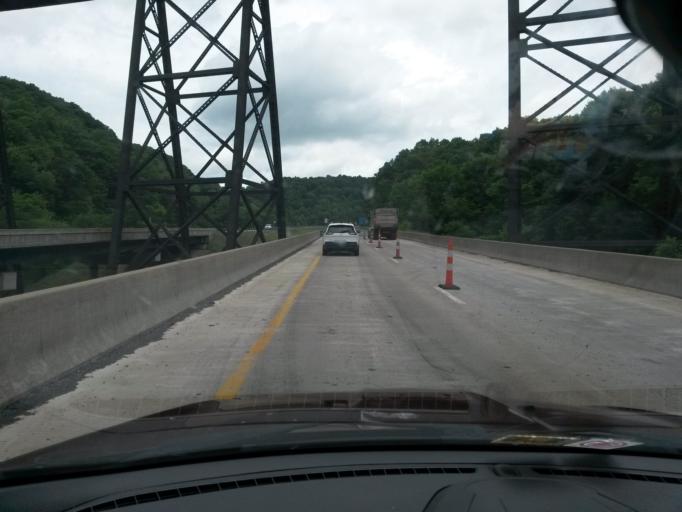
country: US
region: West Virginia
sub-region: Mercer County
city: Princeton
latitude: 37.3391
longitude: -81.0607
